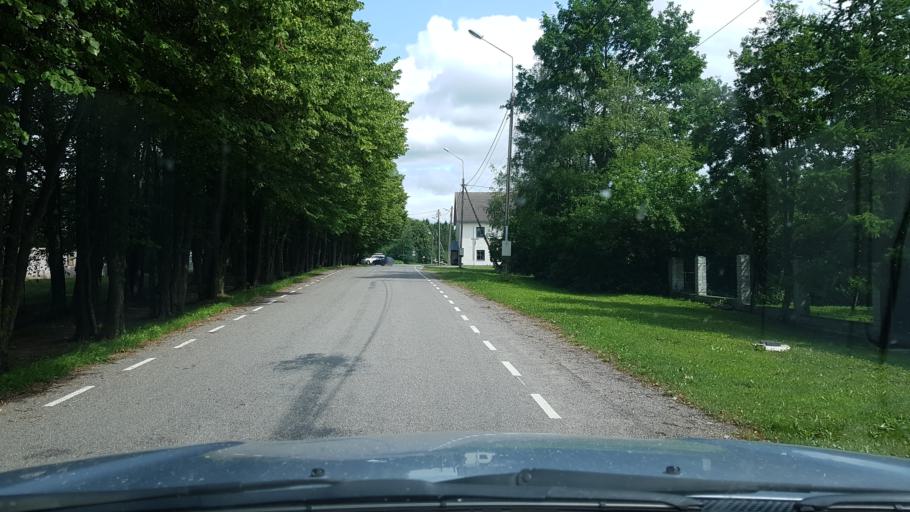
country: EE
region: Ida-Virumaa
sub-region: Sillamaee linn
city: Sillamae
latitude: 59.3731
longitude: 27.8721
